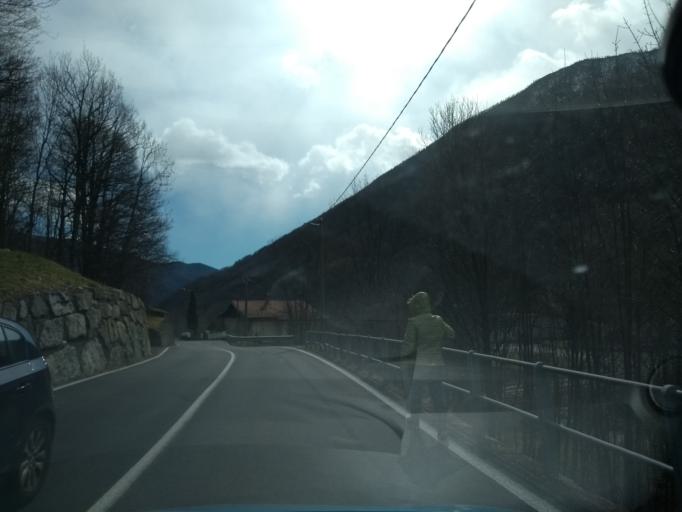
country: IT
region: Piedmont
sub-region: Provincia di Torino
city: Chialamberto
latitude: 45.3664
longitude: 7.3320
